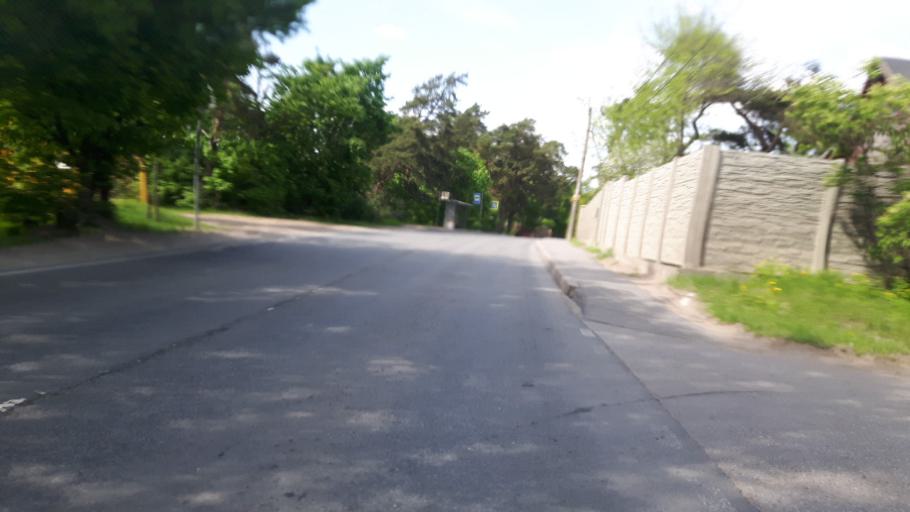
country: RU
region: Leningrad
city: Gorskaya
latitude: 60.0445
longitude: 29.9772
